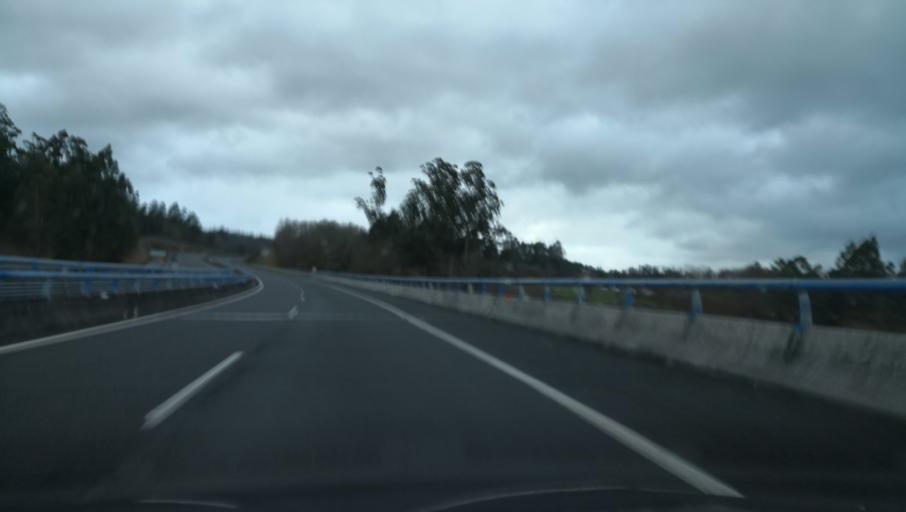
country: ES
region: Galicia
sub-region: Provincia da Coruna
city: Vedra
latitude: 42.8120
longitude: -8.4823
